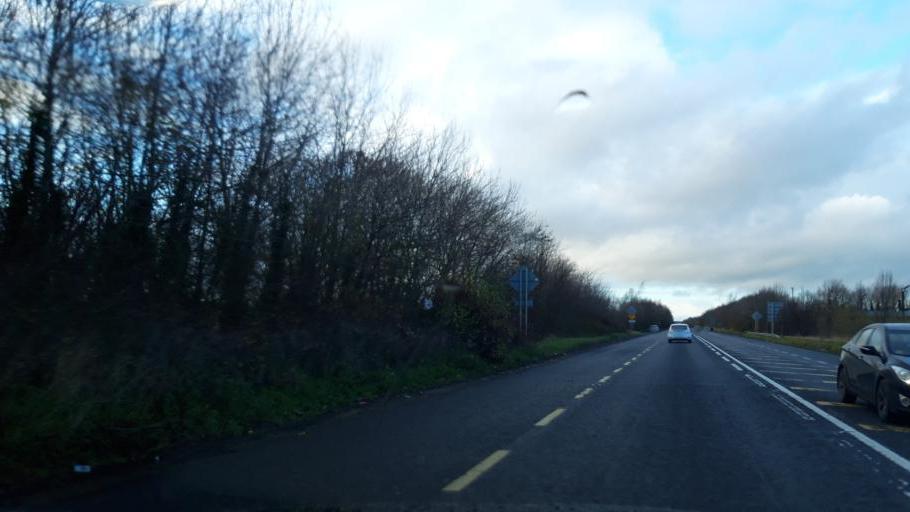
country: IE
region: Leinster
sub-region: Lu
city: Ardee
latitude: 53.8659
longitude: -6.5442
